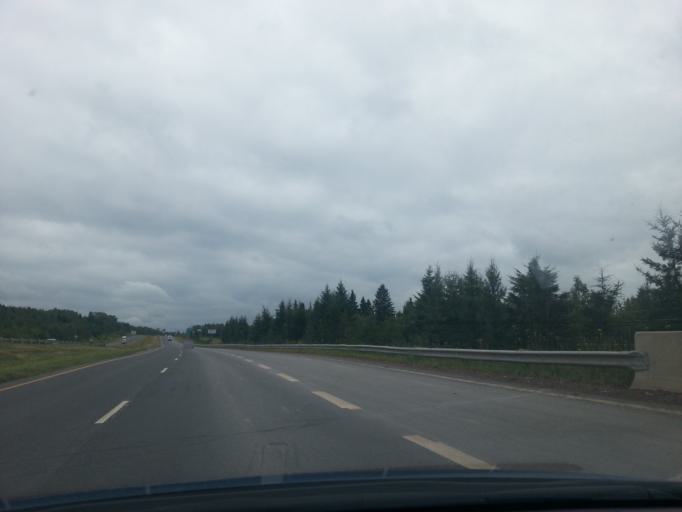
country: CA
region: New Brunswick
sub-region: Madawaska County
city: Saint-Leonard
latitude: 47.1831
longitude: -67.9298
